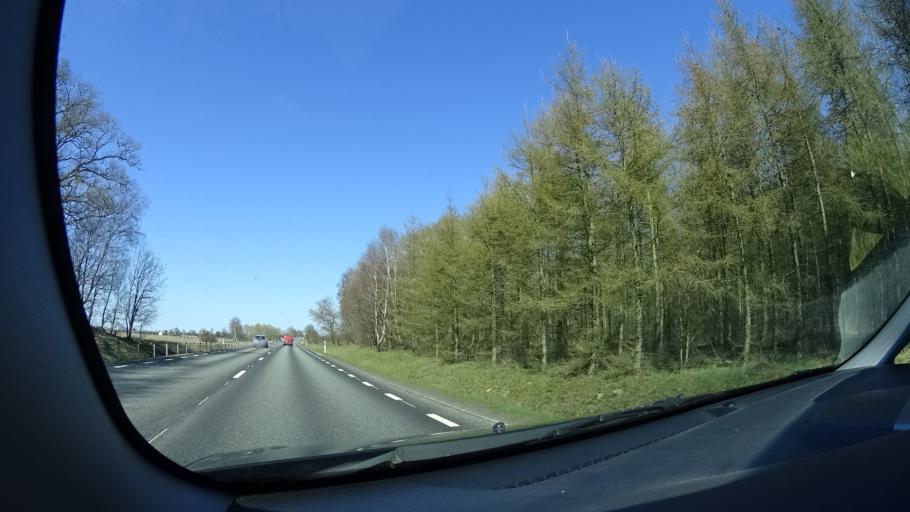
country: SE
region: Skane
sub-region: Angelholms Kommun
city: Strovelstorp
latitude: 56.2014
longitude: 12.7975
